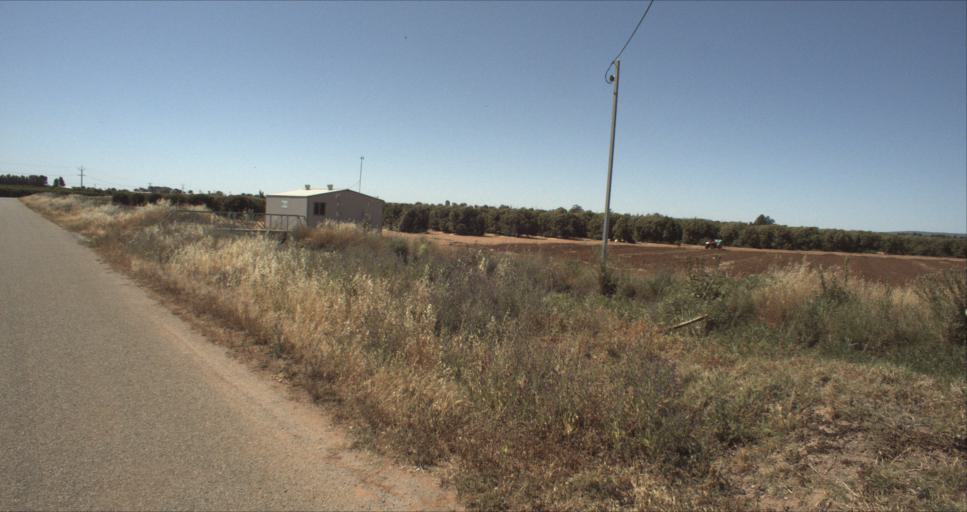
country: AU
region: New South Wales
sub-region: Leeton
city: Leeton
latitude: -34.5402
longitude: 146.3523
